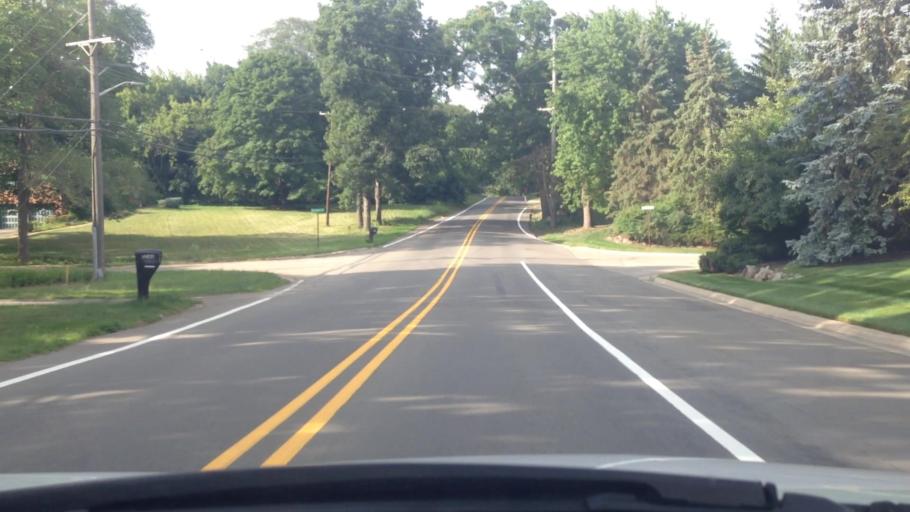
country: US
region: Michigan
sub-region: Oakland County
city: Pontiac
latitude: 42.6762
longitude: -83.3340
